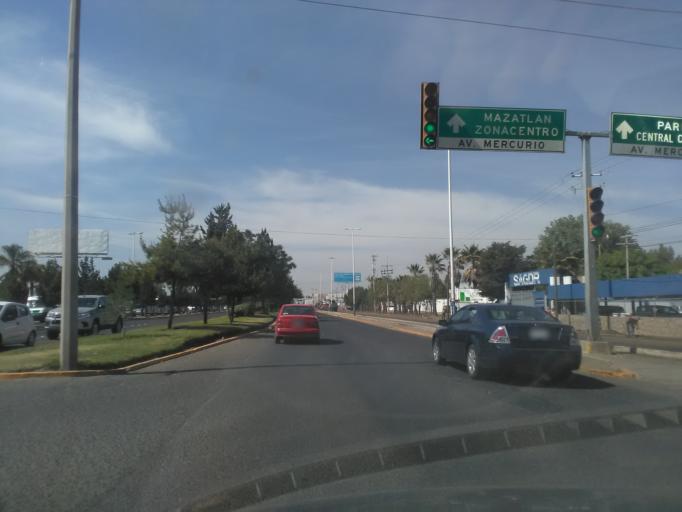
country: MX
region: Durango
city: Victoria de Durango
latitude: 24.0607
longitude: -104.6086
